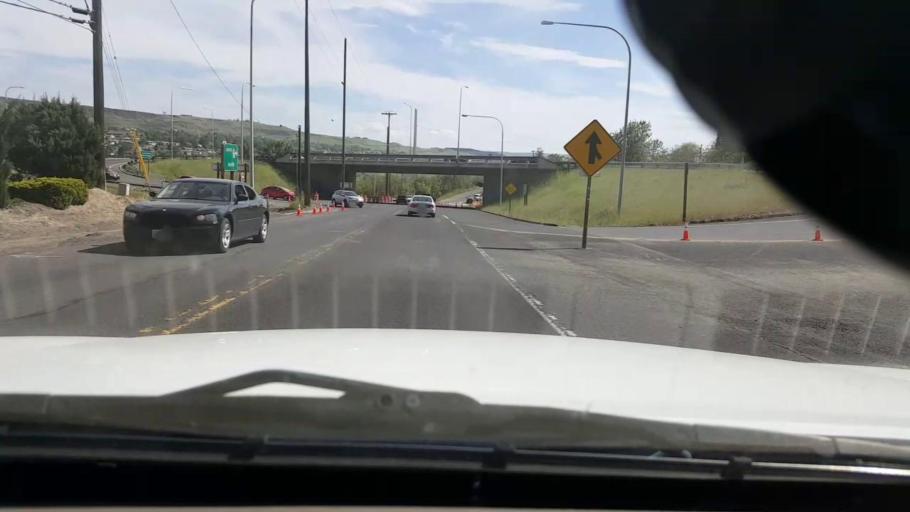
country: US
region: Washington
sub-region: Asotin County
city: Clarkston
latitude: 46.3982
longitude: -117.0443
